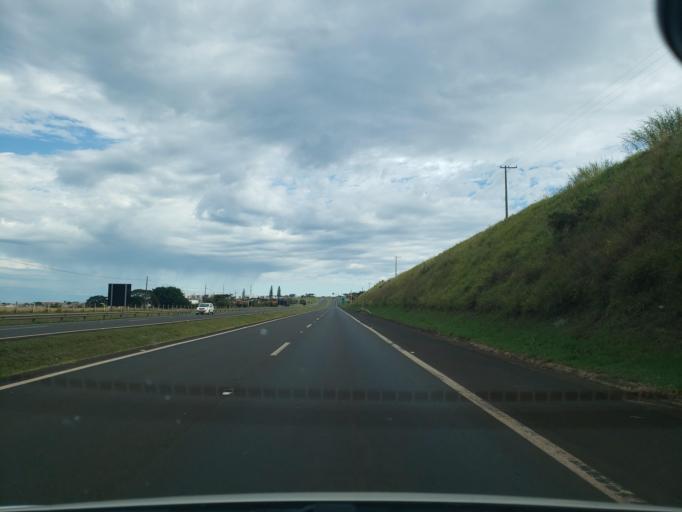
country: BR
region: Sao Paulo
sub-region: Jau
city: Jau
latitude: -22.2607
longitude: -48.5369
